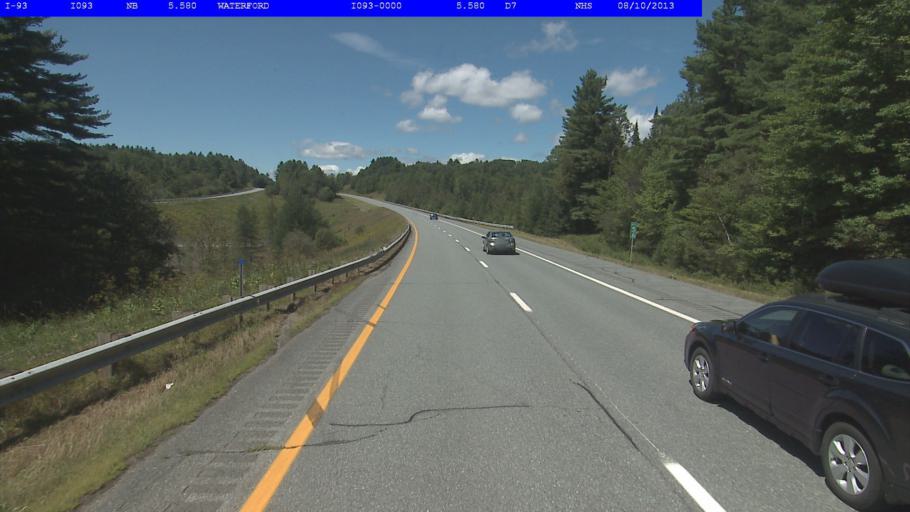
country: US
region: Vermont
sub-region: Caledonia County
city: Saint Johnsbury
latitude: 44.4151
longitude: -71.9238
